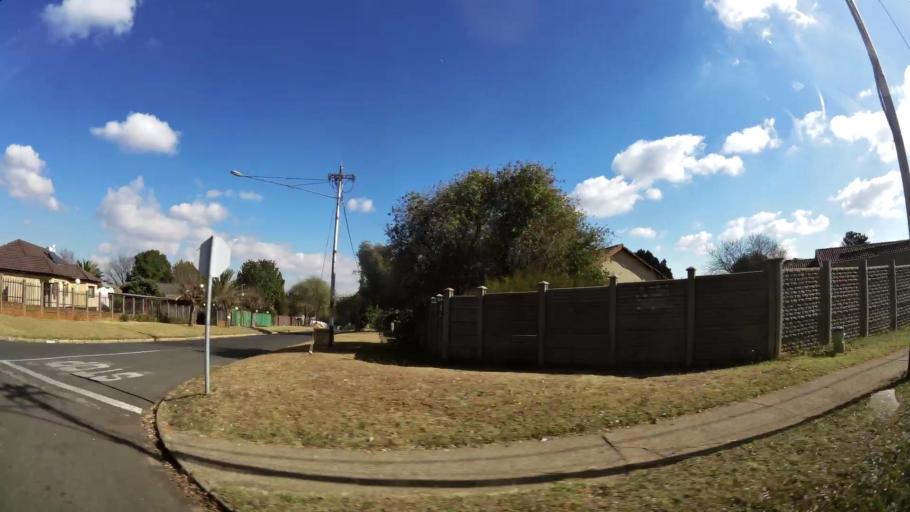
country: ZA
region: Gauteng
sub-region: City of Johannesburg Metropolitan Municipality
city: Roodepoort
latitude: -26.1337
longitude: 27.8313
